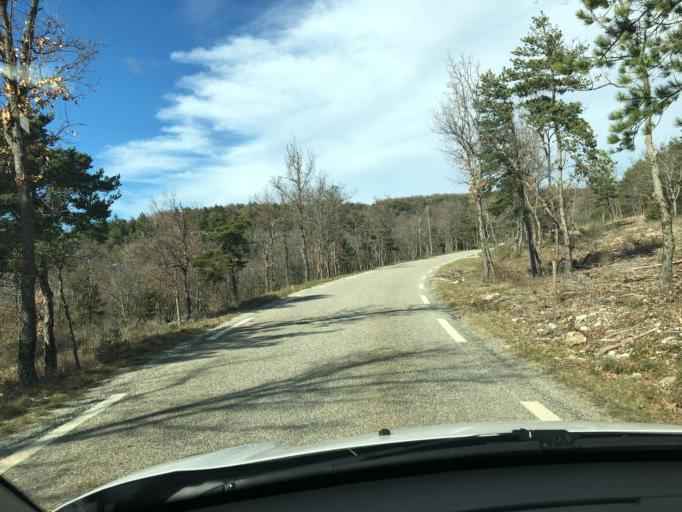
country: FR
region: Provence-Alpes-Cote d'Azur
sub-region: Departement du Vaucluse
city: Saint-Saturnin-les-Apt
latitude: 43.9670
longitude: 5.4623
